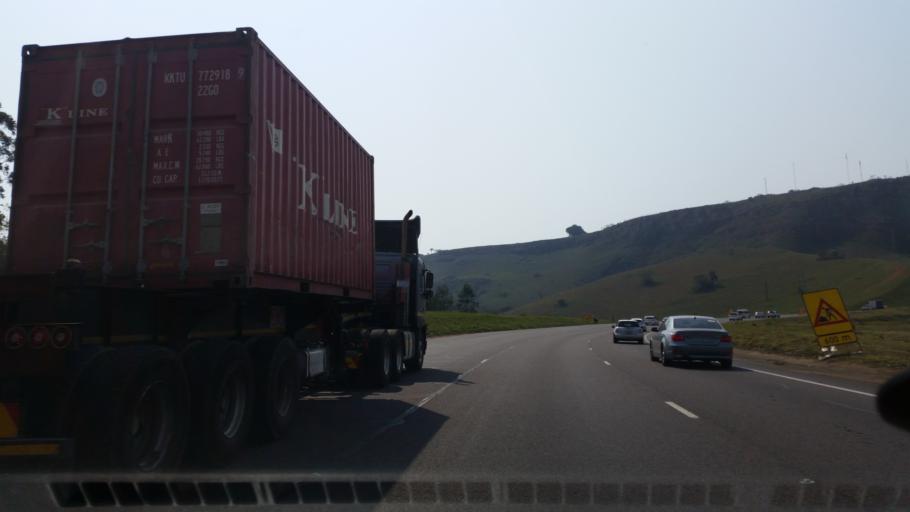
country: ZA
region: KwaZulu-Natal
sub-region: eThekwini Metropolitan Municipality
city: Mpumalanga
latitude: -29.7774
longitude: 30.7045
